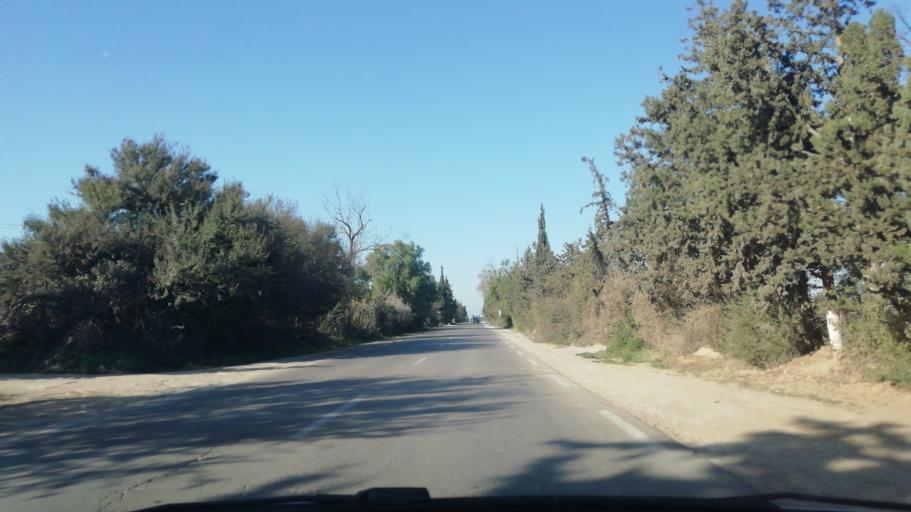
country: DZ
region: Mascara
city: Sig
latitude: 35.5783
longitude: 0.0087
